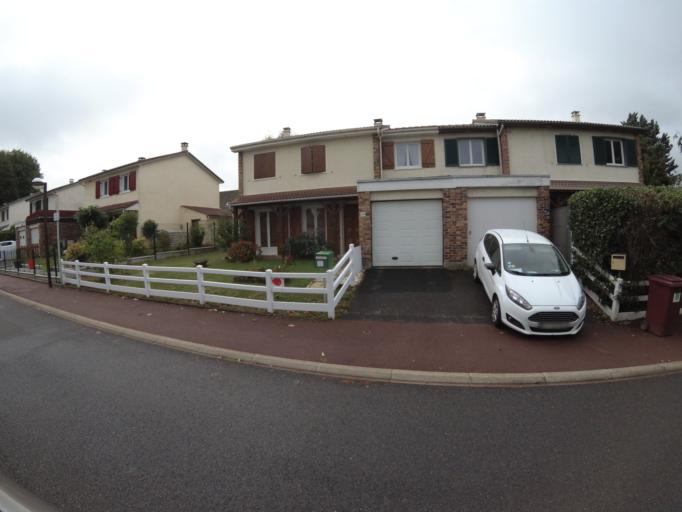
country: FR
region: Ile-de-France
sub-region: Departement de Seine-et-Marne
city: Conches-sur-Gondoire
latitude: 48.8539
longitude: 2.7164
